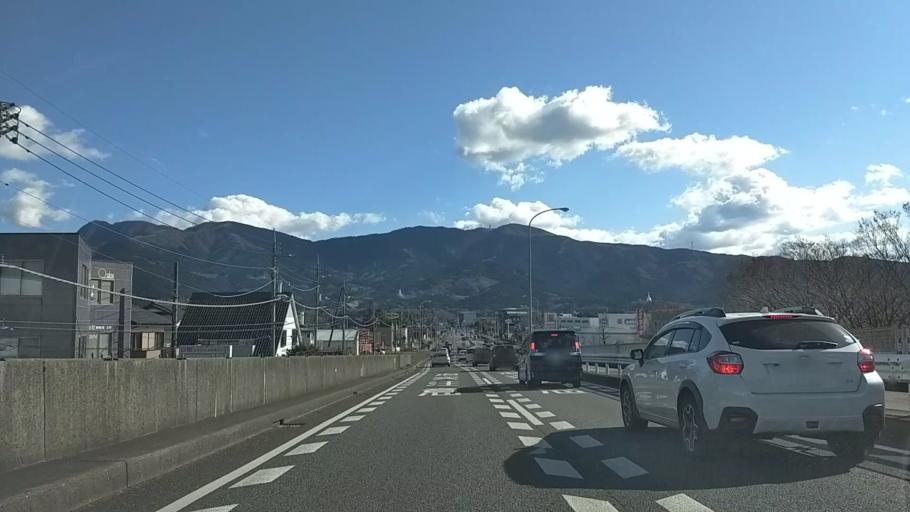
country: JP
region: Shizuoka
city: Gotemba
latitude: 35.3053
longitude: 138.9408
